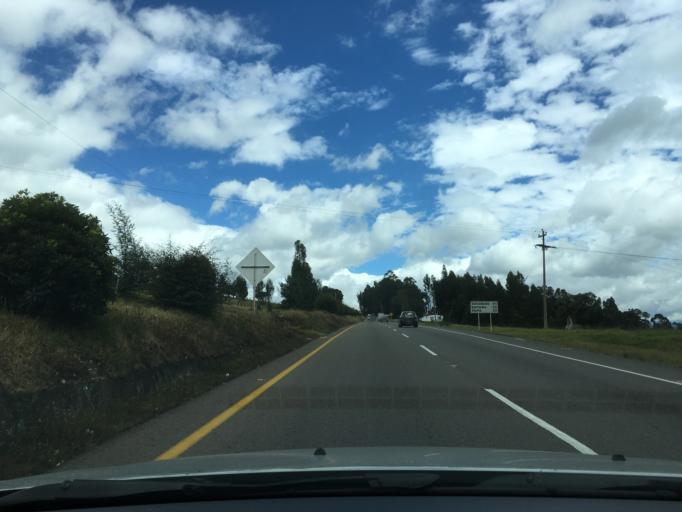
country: CO
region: Boyaca
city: Tuta
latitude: 5.6667
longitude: -73.2702
